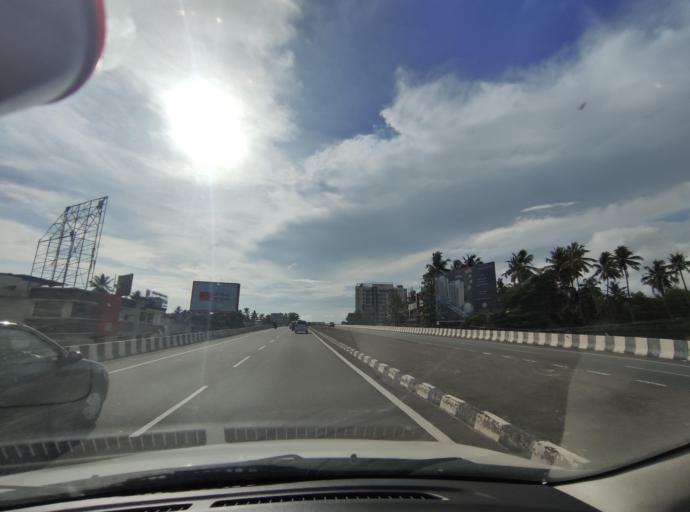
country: IN
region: Kerala
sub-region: Thiruvananthapuram
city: Thiruvananthapuram
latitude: 8.5081
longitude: 76.9060
